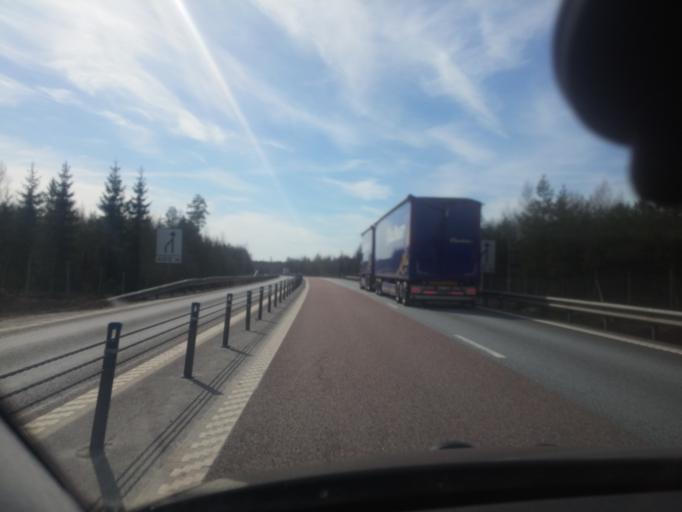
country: SE
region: Gaevleborg
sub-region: Gavle Kommun
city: Gavle
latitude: 60.7830
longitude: 17.0741
